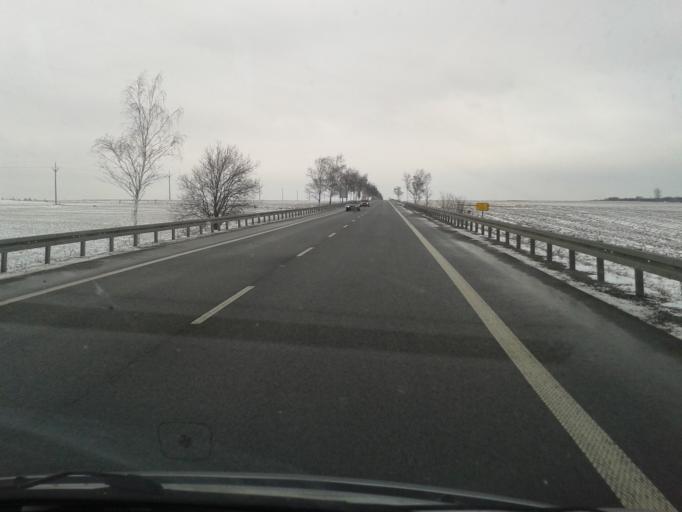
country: SK
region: Zilinsky
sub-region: Okres Zilina
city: Trstena
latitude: 49.3825
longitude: 19.6340
